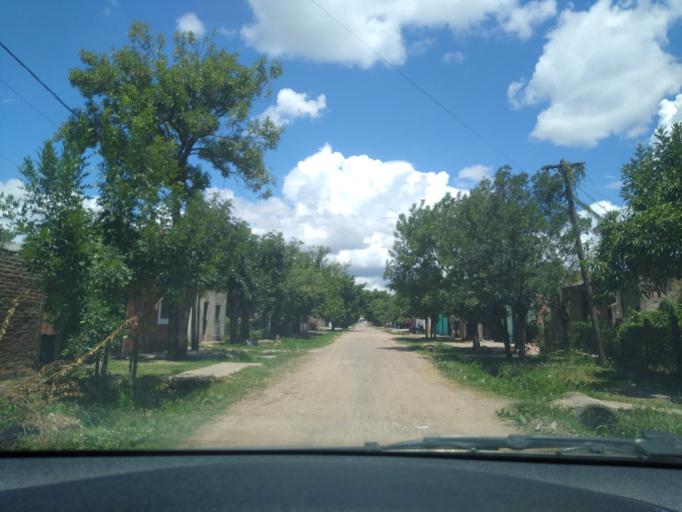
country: AR
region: Chaco
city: Barranqueras
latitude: -27.4725
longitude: -58.9296
